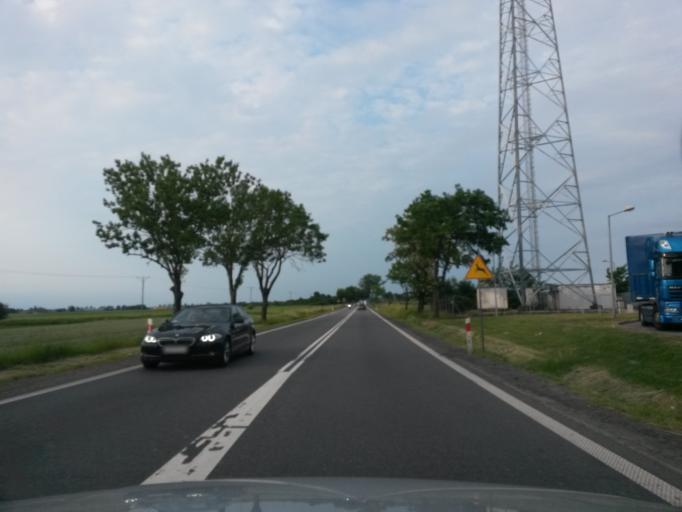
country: PL
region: Lower Silesian Voivodeship
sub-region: Powiat sredzki
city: Ciechow
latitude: 51.0381
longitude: 16.5845
